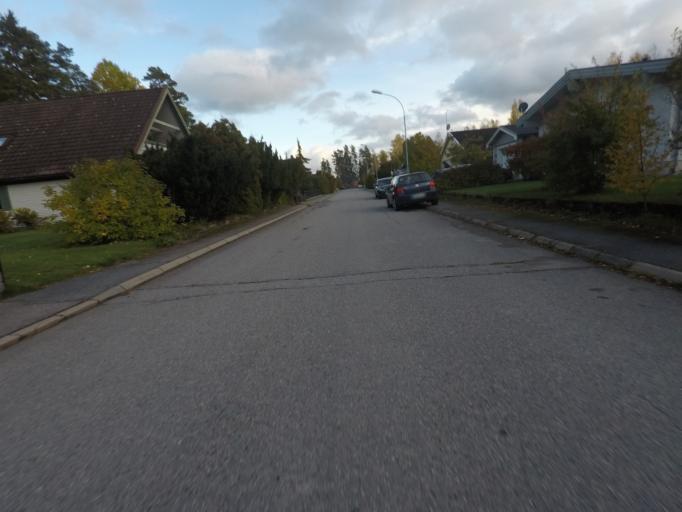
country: SE
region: OErebro
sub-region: Karlskoga Kommun
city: Karlskoga
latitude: 59.3061
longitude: 14.4879
